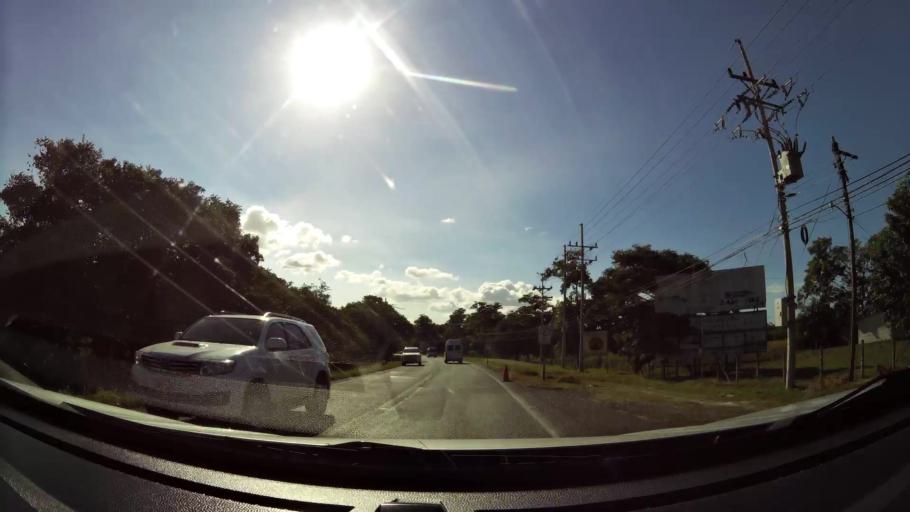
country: CR
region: Guanacaste
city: Sardinal
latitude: 10.5795
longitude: -85.5776
